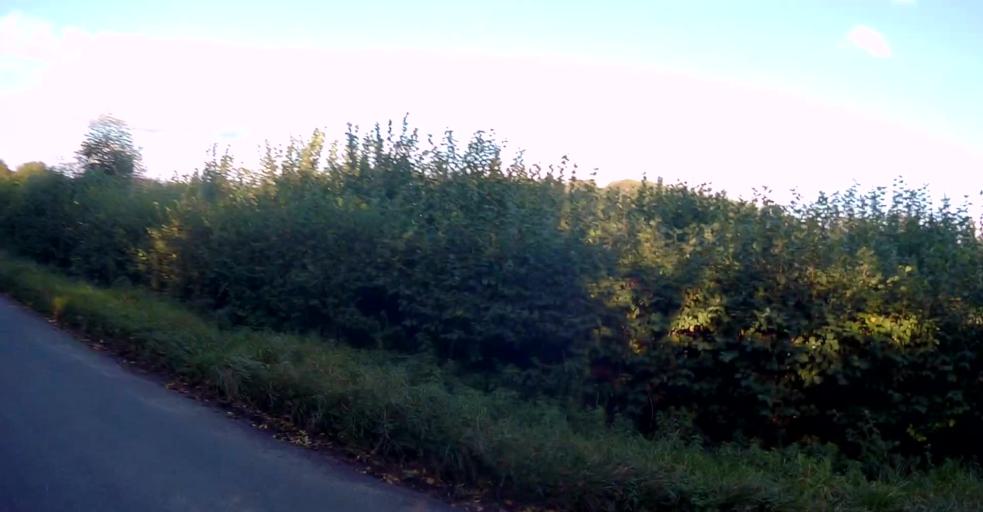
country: GB
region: England
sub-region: Hampshire
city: Long Sutton
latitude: 51.2304
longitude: -0.9258
